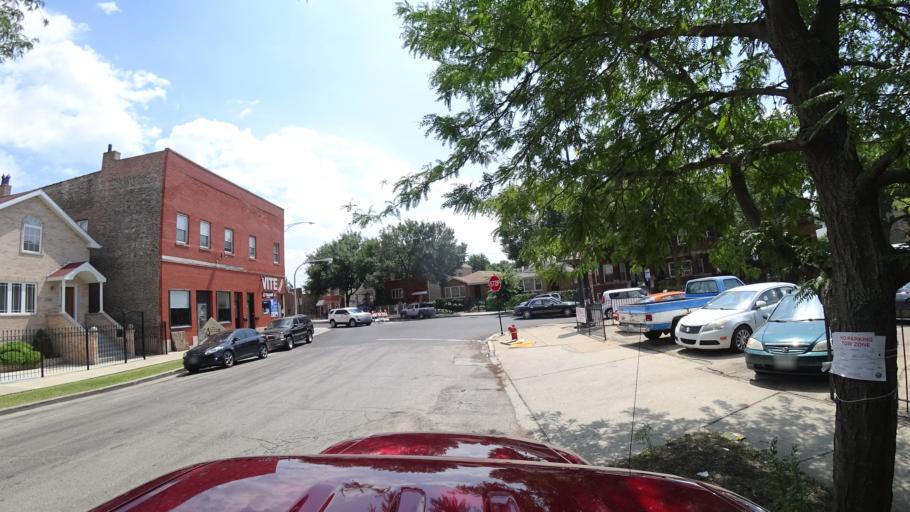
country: US
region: Illinois
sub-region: Cook County
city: Chicago
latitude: 41.8383
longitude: -87.6497
